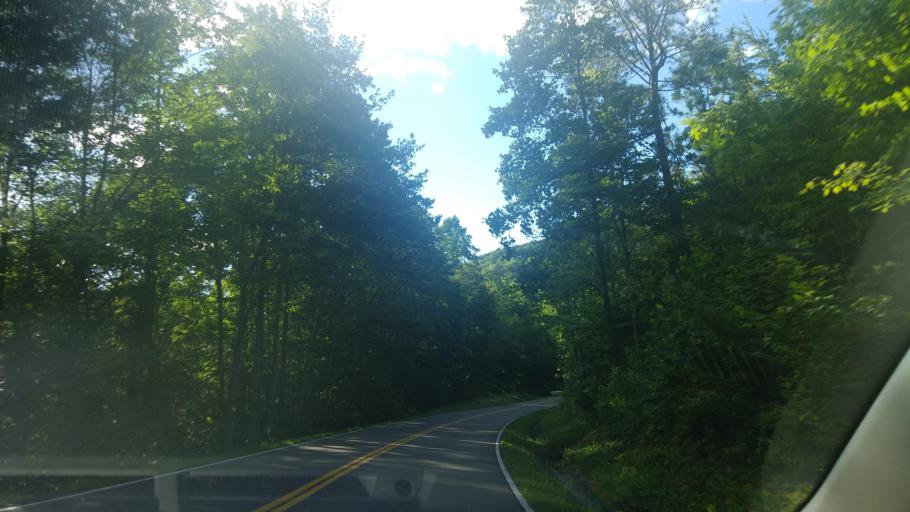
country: US
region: Tennessee
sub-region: Cocke County
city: Newport
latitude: 35.8192
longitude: -83.2151
